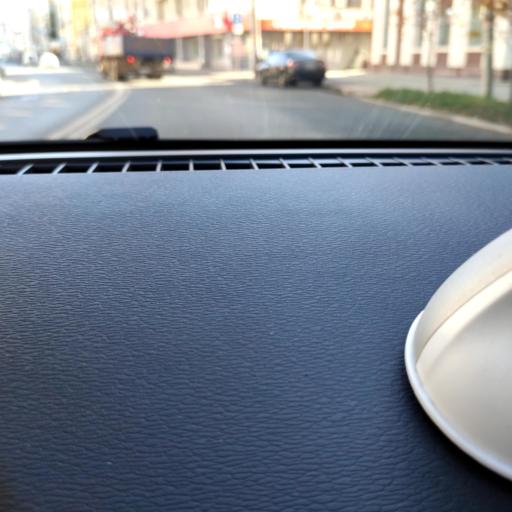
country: RU
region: Samara
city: Samara
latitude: 53.1869
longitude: 50.1162
